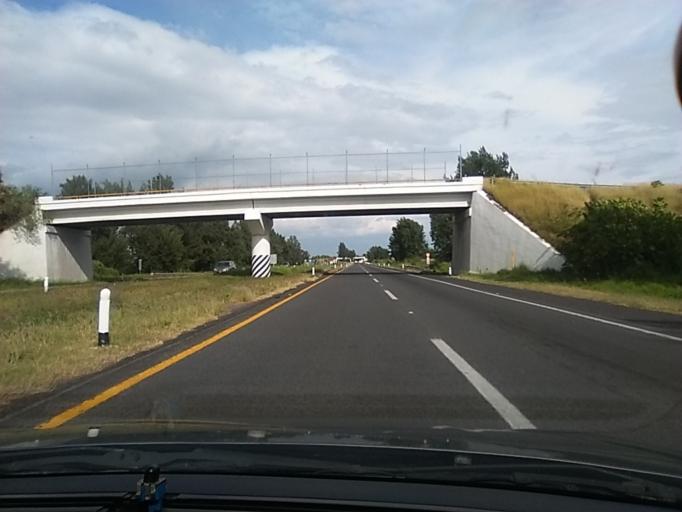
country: MX
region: Jalisco
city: La Barca
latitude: 20.3219
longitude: -102.5165
